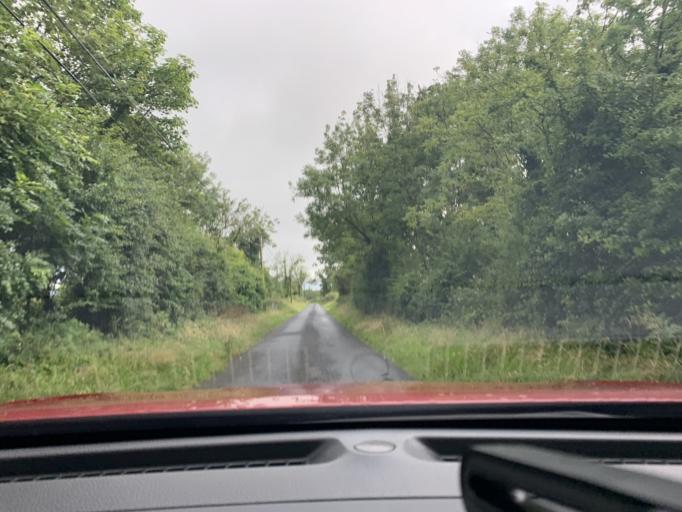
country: IE
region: Connaught
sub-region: Sligo
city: Strandhill
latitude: 54.3618
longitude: -8.5312
